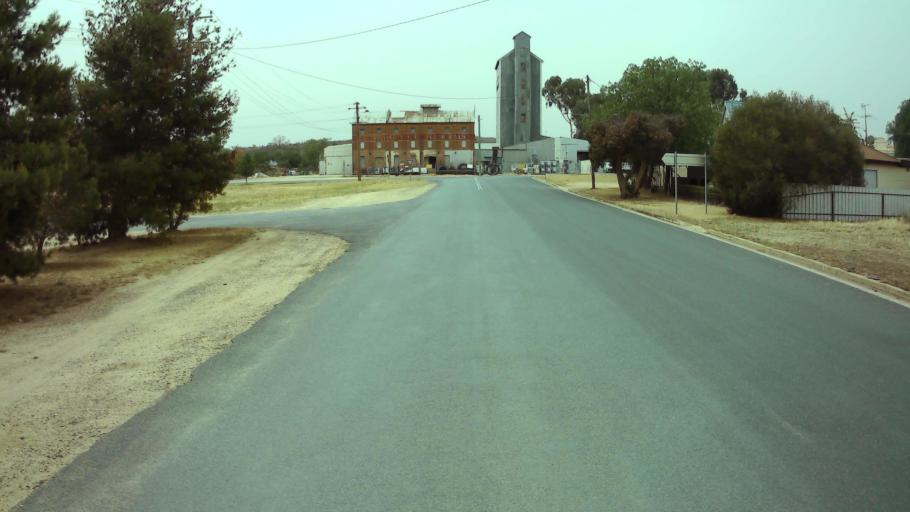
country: AU
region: New South Wales
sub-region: Weddin
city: Grenfell
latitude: -33.8957
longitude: 148.1561
